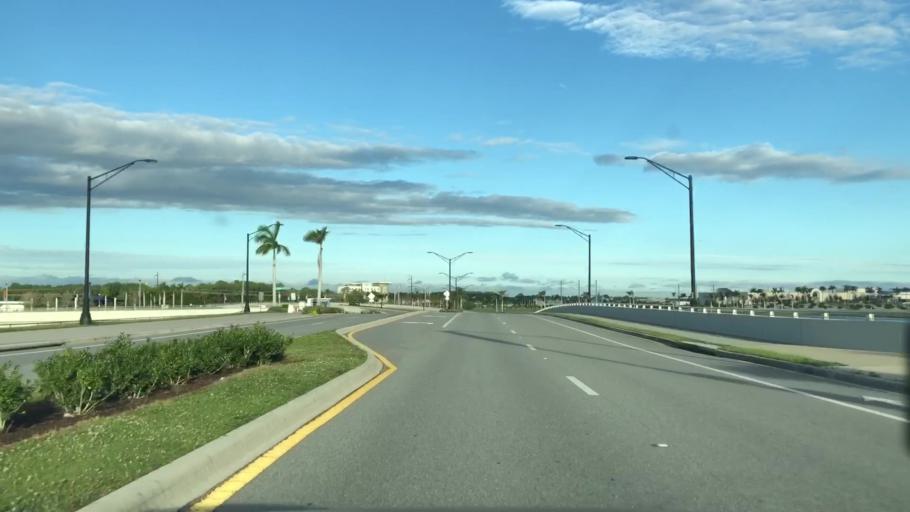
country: US
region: Florida
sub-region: Sarasota County
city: The Meadows
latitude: 27.3761
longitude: -82.4502
